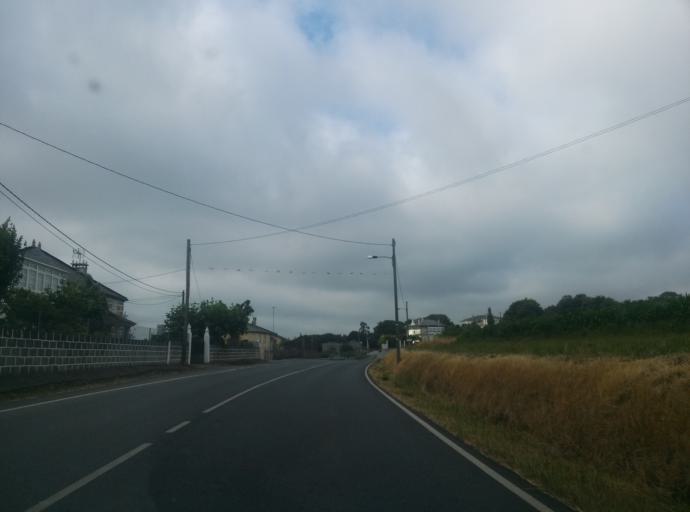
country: ES
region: Galicia
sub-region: Provincia de Lugo
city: Lugo
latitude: 43.0602
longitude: -7.5664
